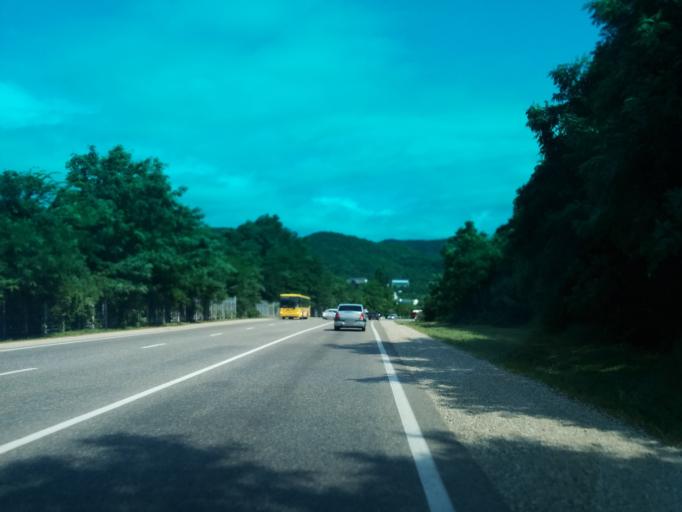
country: RU
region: Krasnodarskiy
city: Nebug
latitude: 44.1593
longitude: 39.0018
